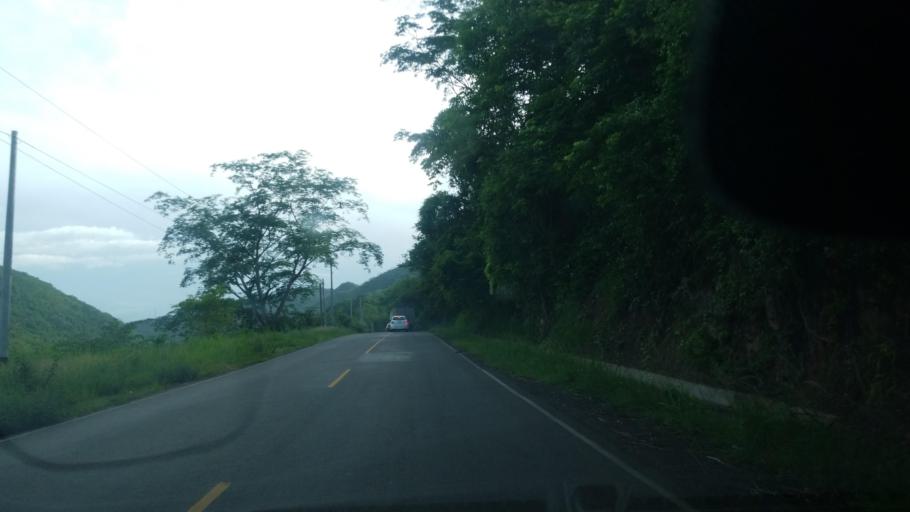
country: HN
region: Santa Barbara
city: Ilama
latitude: 15.0896
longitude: -88.2113
